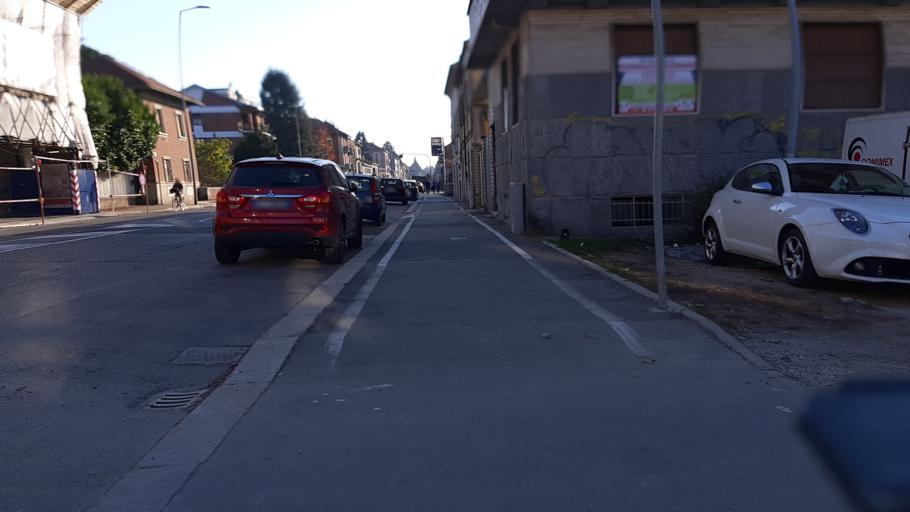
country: IT
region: Piedmont
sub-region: Provincia di Torino
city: Moncalieri
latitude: 45.0358
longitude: 7.6805
